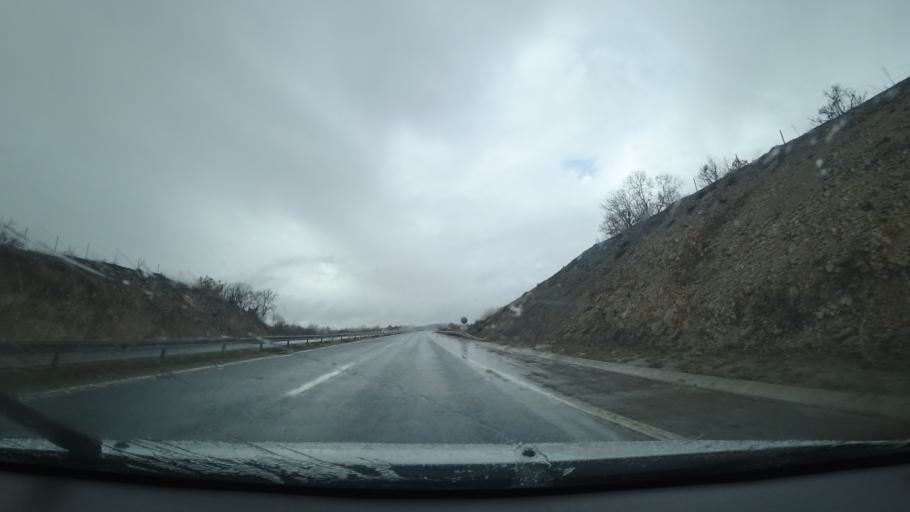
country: HR
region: Licko-Senjska
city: Gospic
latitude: 44.6729
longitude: 15.4164
